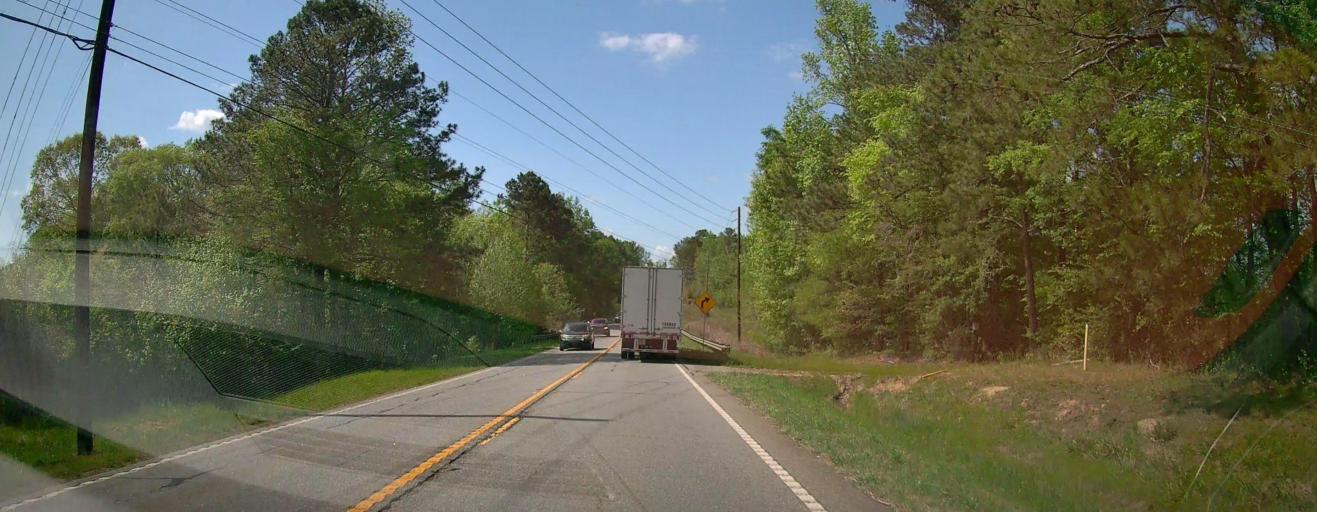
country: US
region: Georgia
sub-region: Greene County
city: Greensboro
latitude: 33.5054
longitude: -83.2252
